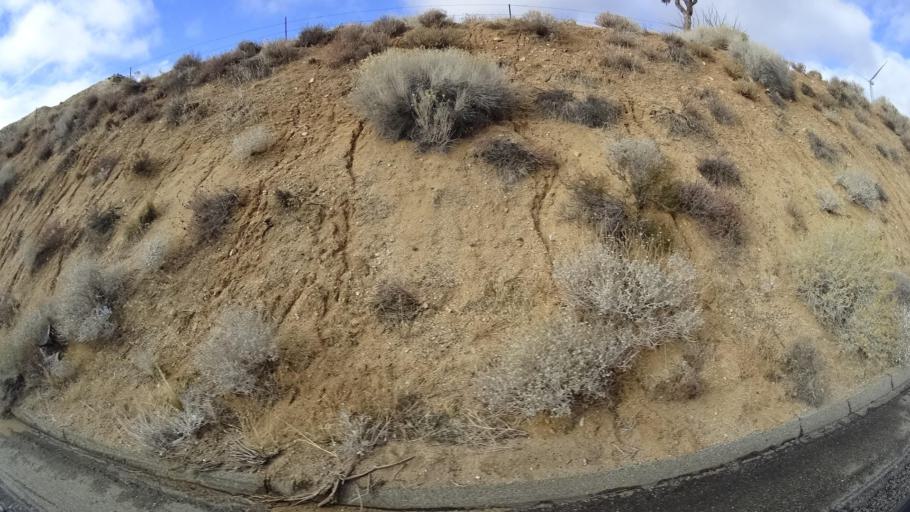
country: US
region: California
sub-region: Kern County
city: Tehachapi
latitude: 35.0217
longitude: -118.3504
